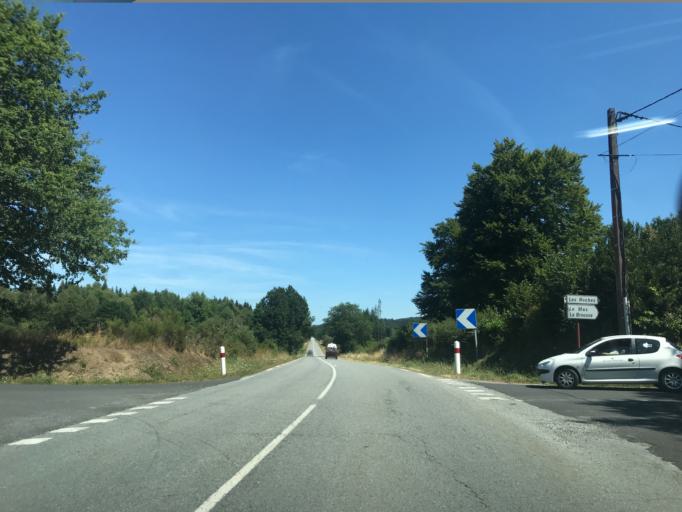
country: FR
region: Limousin
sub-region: Departement de la Correze
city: Meymac
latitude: 45.4917
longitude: 2.2098
